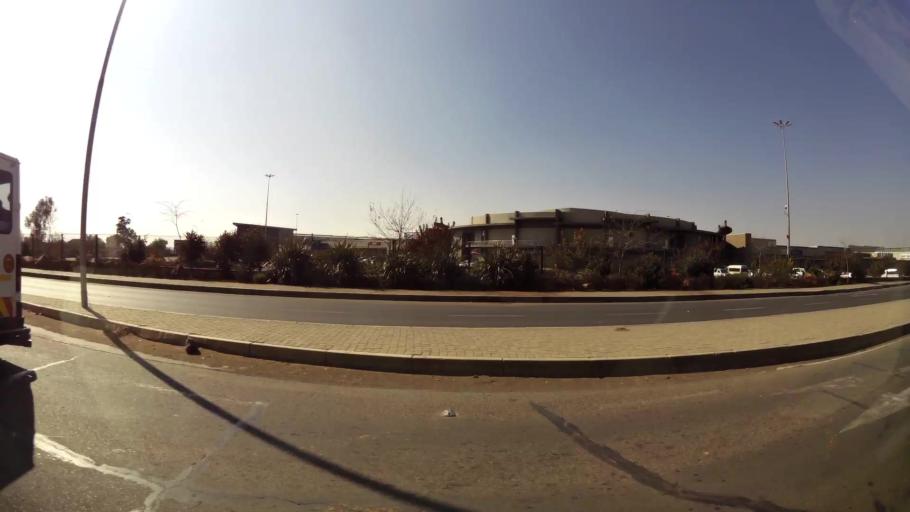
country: ZA
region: Orange Free State
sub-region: Mangaung Metropolitan Municipality
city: Bloemfontein
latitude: -29.1583
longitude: 26.2550
